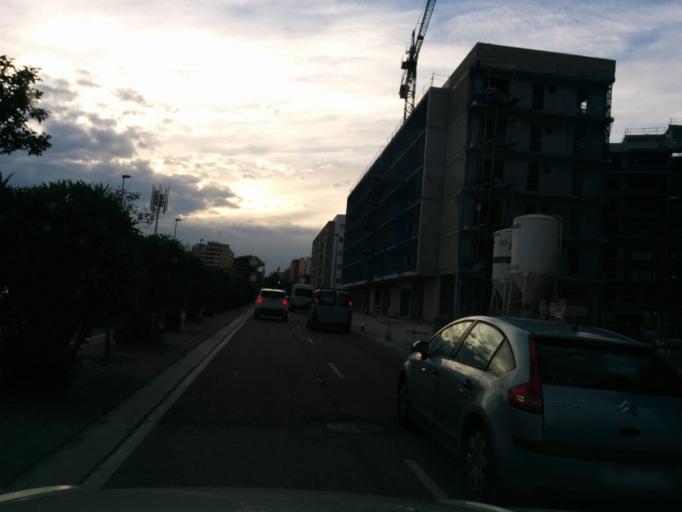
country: ES
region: Aragon
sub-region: Provincia de Zaragoza
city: Zaragoza
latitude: 41.6359
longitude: -0.8652
